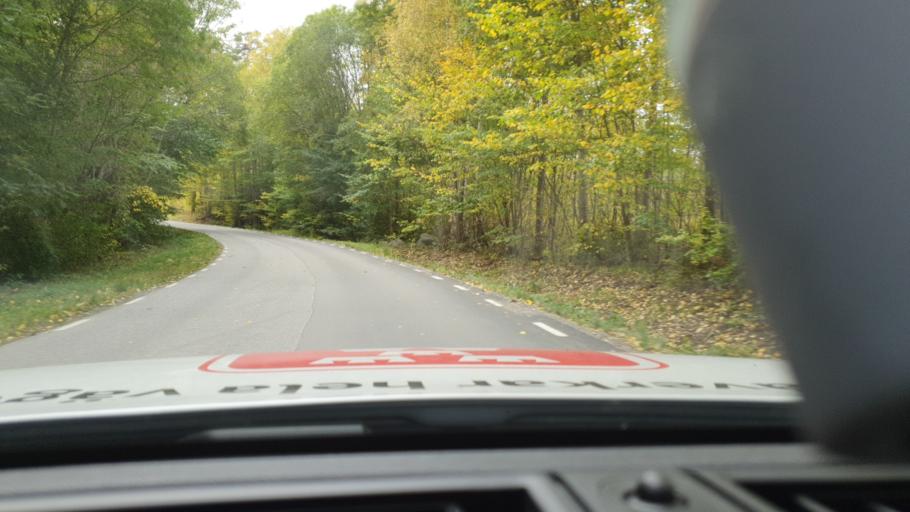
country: SE
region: Stockholm
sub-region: Upplands-Bro Kommun
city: Bro
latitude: 59.4923
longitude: 17.5679
